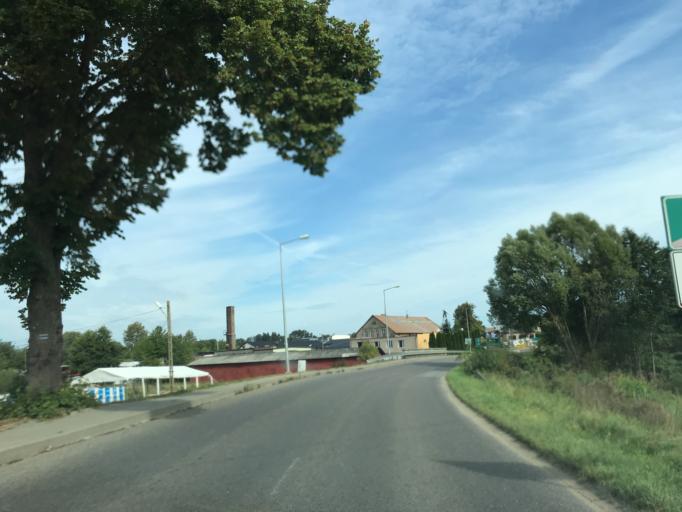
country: PL
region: Pomeranian Voivodeship
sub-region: Powiat pucki
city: Krokowa
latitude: 54.7810
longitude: 18.1688
